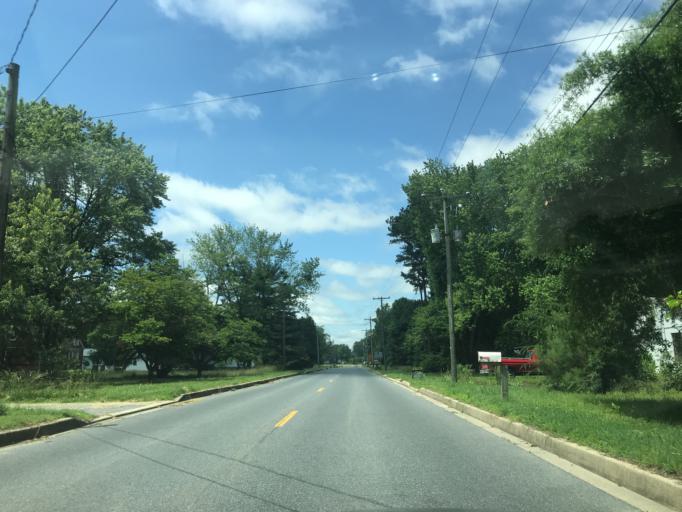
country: US
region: Maryland
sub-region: Caroline County
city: Federalsburg
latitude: 38.6901
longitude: -75.7857
